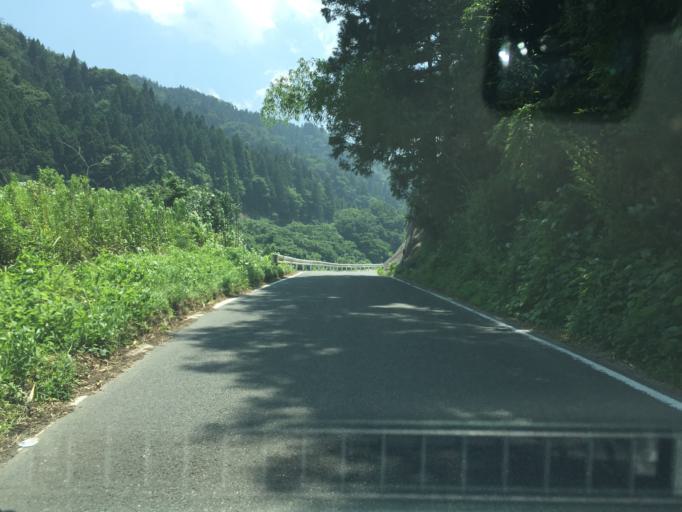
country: JP
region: Miyagi
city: Marumori
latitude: 37.9226
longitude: 140.6894
